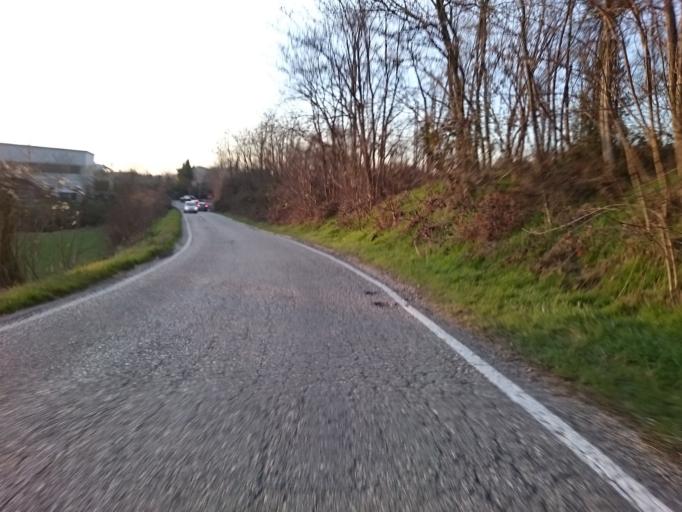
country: IT
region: Veneto
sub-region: Provincia di Verona
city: Castelnuovo del Garda
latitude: 45.4291
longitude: 10.7658
